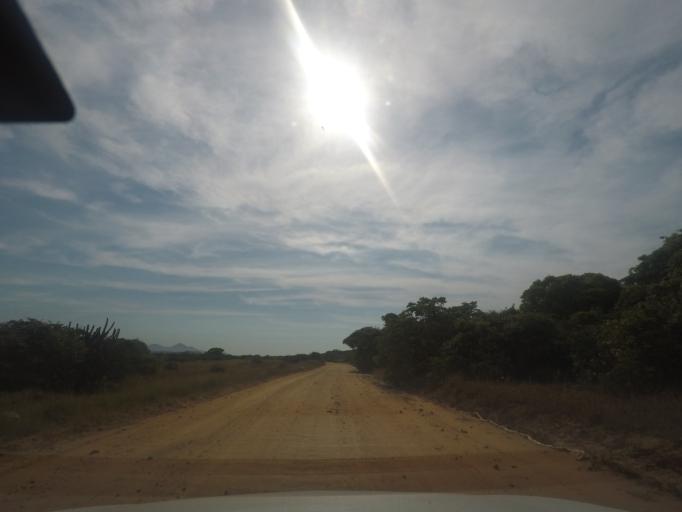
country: BR
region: Rio de Janeiro
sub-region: Marica
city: Marica
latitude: -22.9604
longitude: -42.8612
